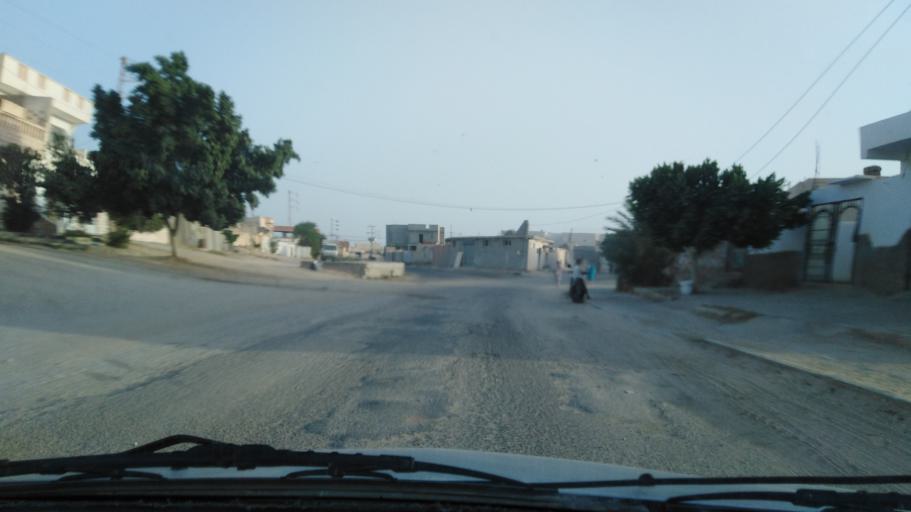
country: TN
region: Qabis
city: Gabes
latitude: 33.9573
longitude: 9.9953
